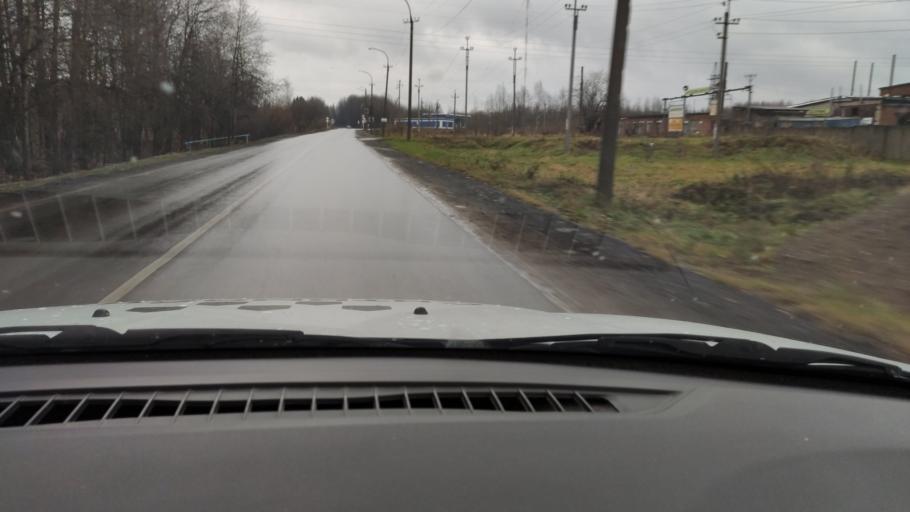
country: RU
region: Perm
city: Sylva
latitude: 58.0280
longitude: 56.7395
